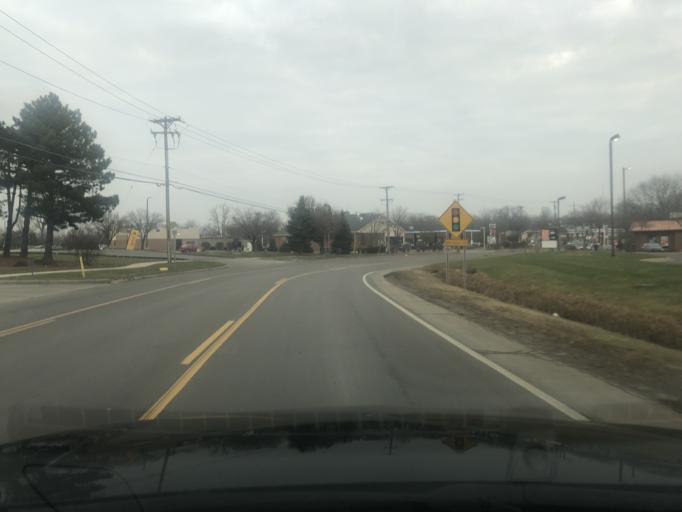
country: US
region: Michigan
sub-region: Wayne County
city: Belleville
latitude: 42.2220
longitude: -83.4871
